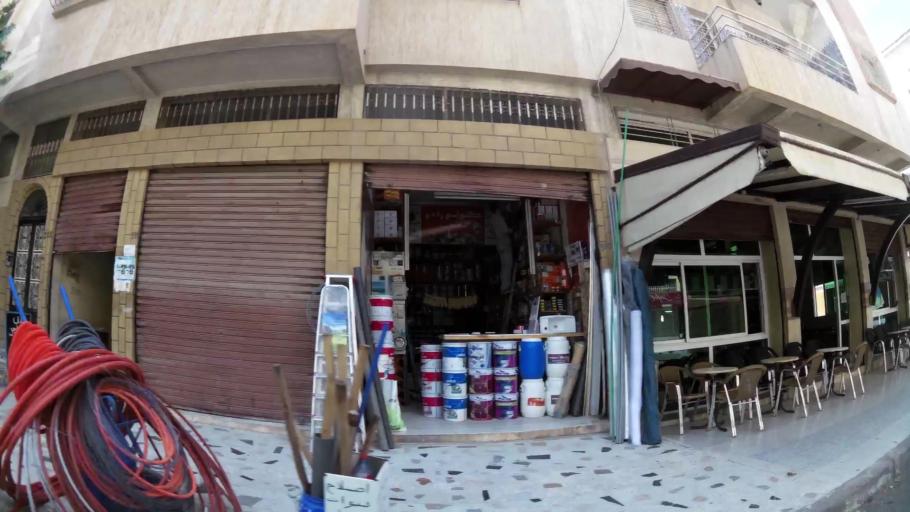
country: MA
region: Fes-Boulemane
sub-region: Fes
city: Fes
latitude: 34.0082
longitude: -4.9877
